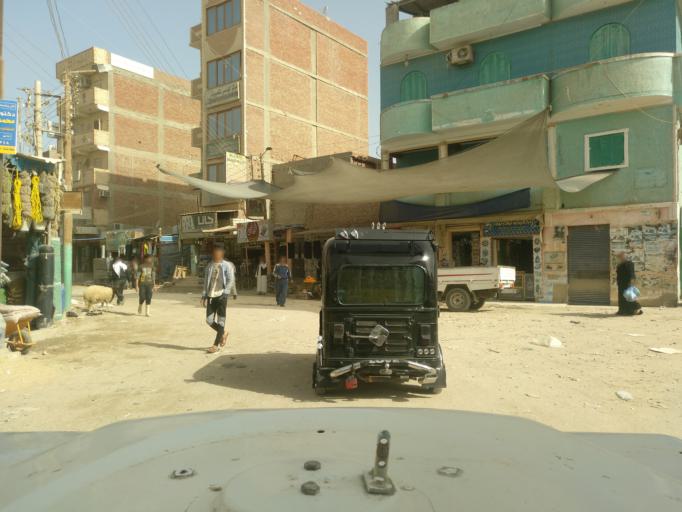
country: EG
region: Al Buhayrah
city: Beheira
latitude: 30.3759
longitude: 30.3488
